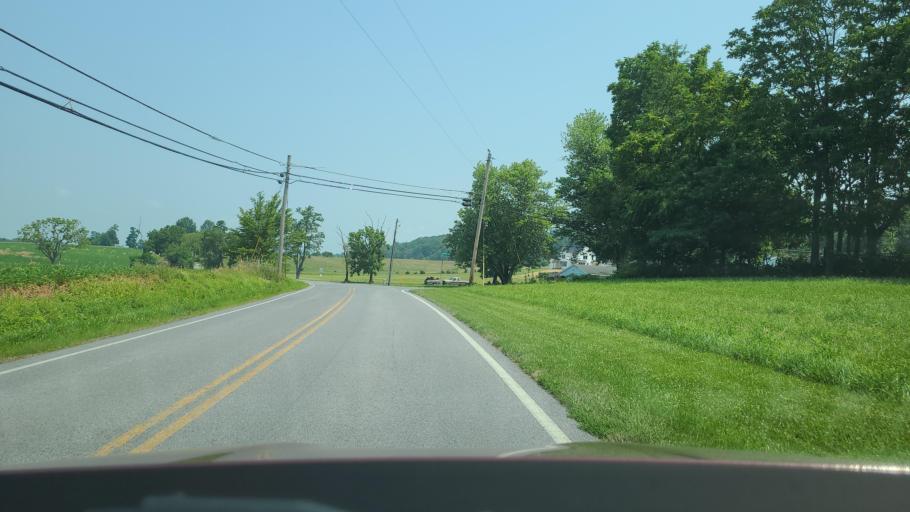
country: US
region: Maryland
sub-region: Frederick County
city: Jefferson
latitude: 39.3797
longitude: -77.5200
